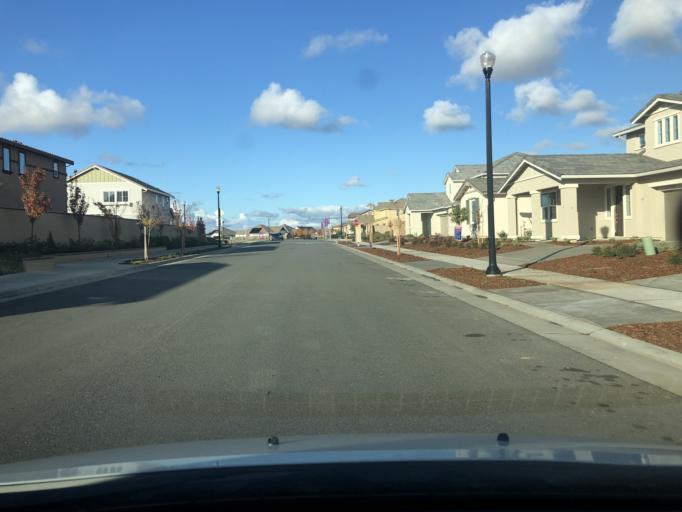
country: US
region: California
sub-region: Sacramento County
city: Antelope
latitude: 38.7702
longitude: -121.3810
